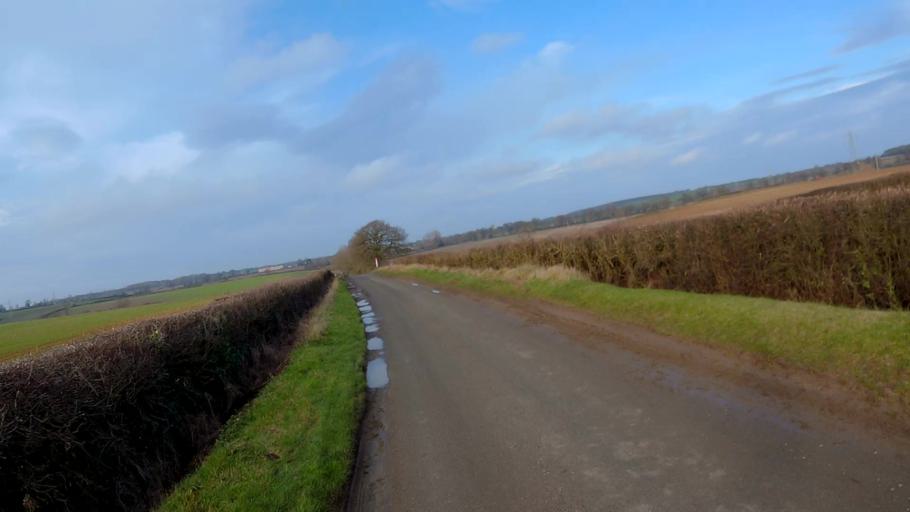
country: GB
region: England
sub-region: Lincolnshire
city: Bourne
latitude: 52.7685
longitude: -0.4225
